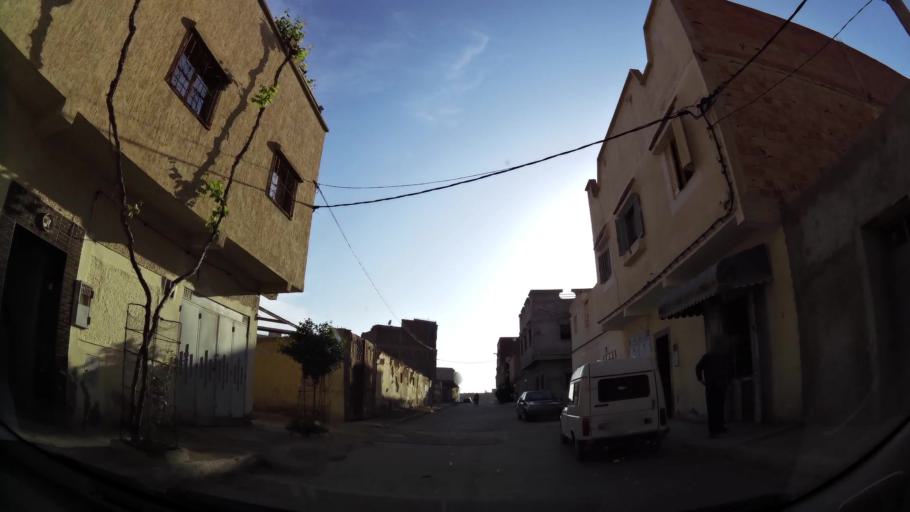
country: MA
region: Oriental
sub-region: Oujda-Angad
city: Oujda
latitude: 34.7042
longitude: -1.8985
